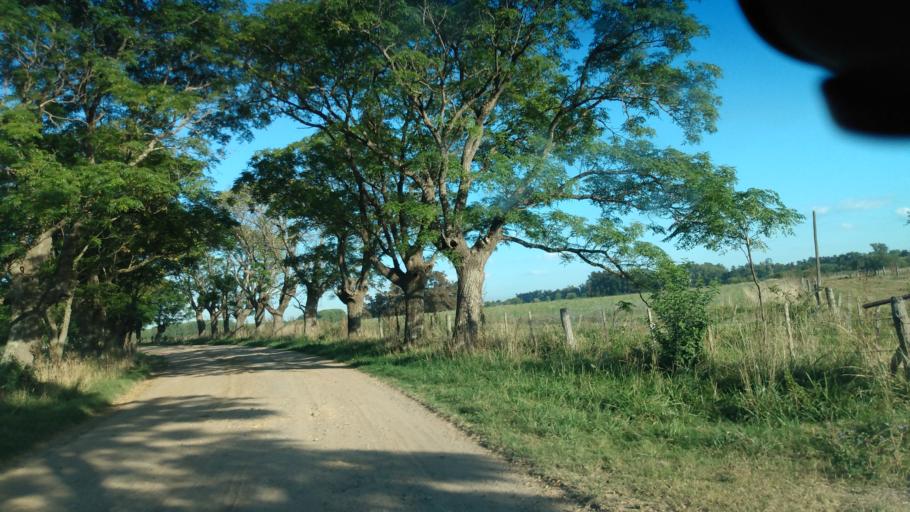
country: AR
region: Buenos Aires
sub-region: Partido de Lujan
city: Lujan
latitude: -34.5875
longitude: -59.0668
